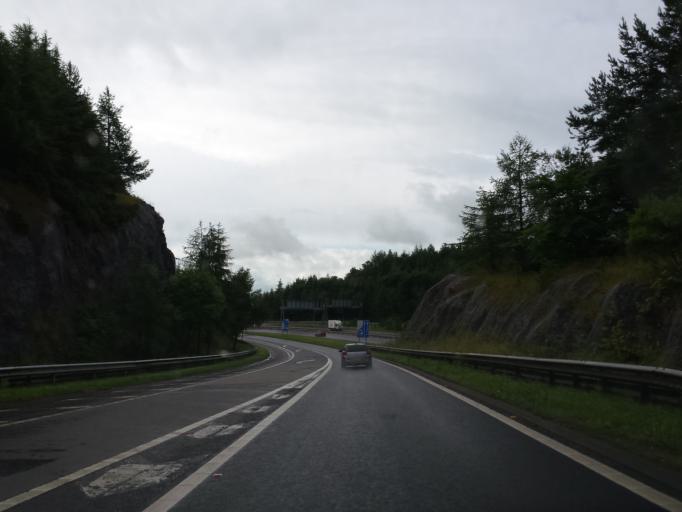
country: GB
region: Scotland
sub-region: Perth and Kinross
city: Bridge of Earn
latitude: 56.3672
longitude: -3.4224
